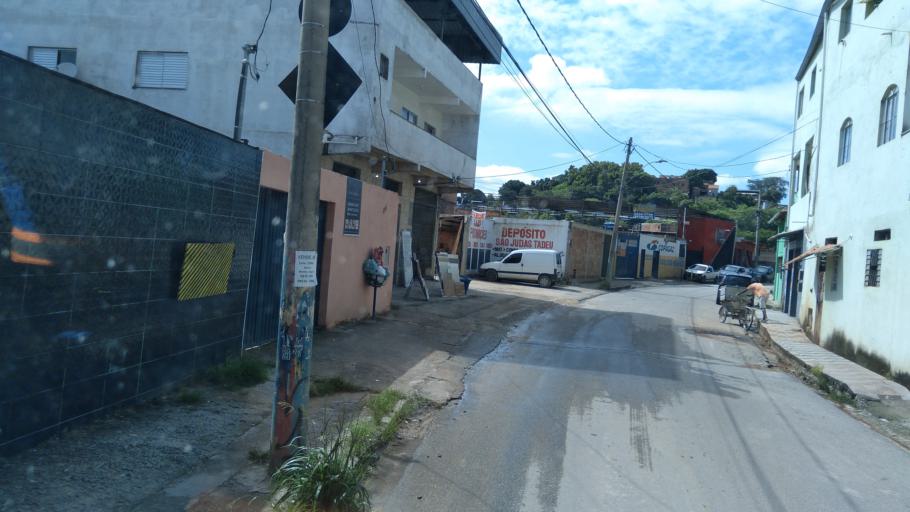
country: BR
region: Minas Gerais
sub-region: Santa Luzia
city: Santa Luzia
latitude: -19.8294
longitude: -43.8945
